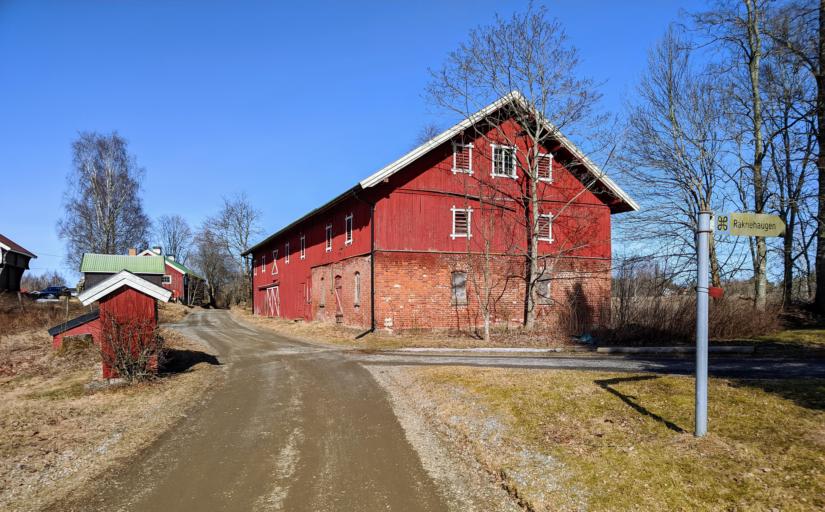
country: NO
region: Akershus
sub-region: Ullensaker
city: Jessheim
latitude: 60.1480
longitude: 11.1345
